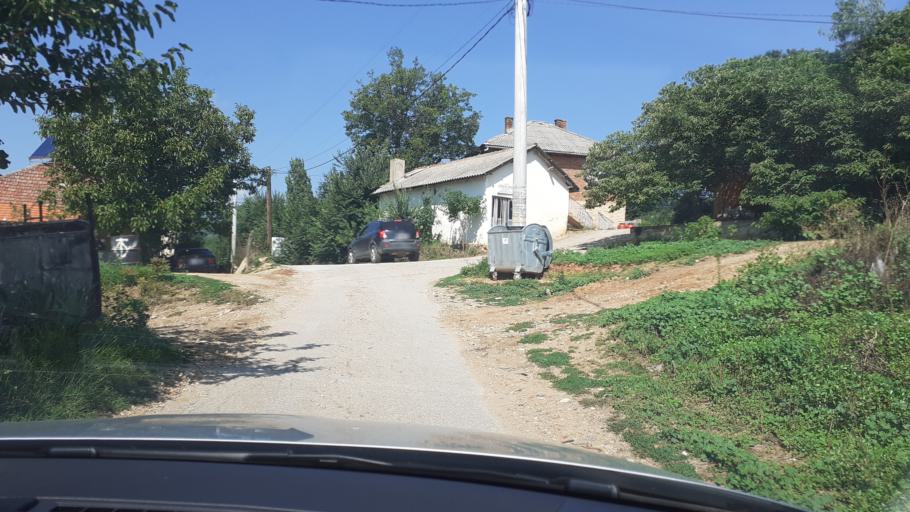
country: MK
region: Strumica
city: Veljusa
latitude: 41.5209
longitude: 22.5921
